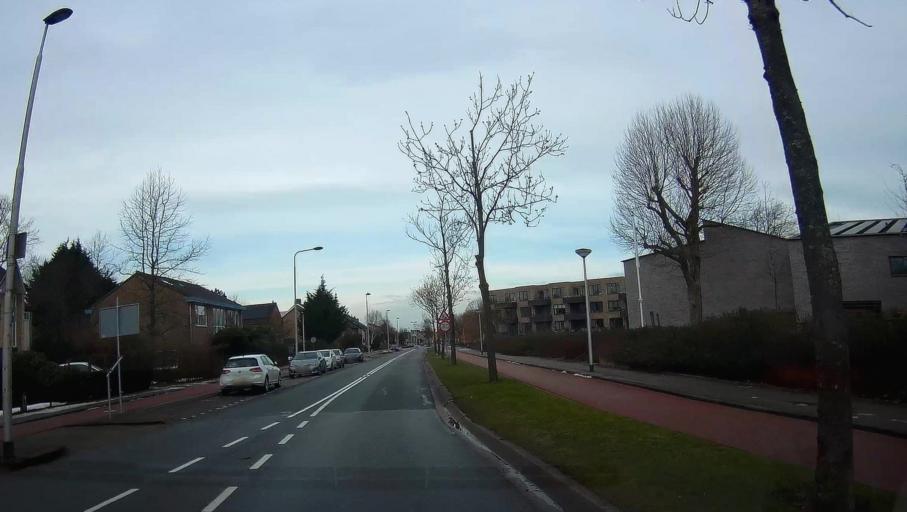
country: NL
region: South Holland
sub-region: Gemeente Barendrecht
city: Barendrecht
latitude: 51.8523
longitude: 4.5469
